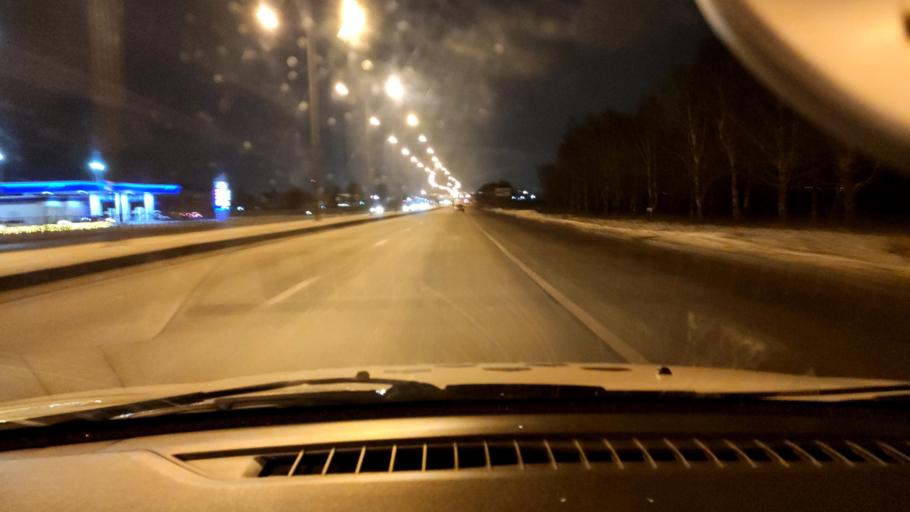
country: RU
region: Perm
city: Kondratovo
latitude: 57.9465
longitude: 56.0833
